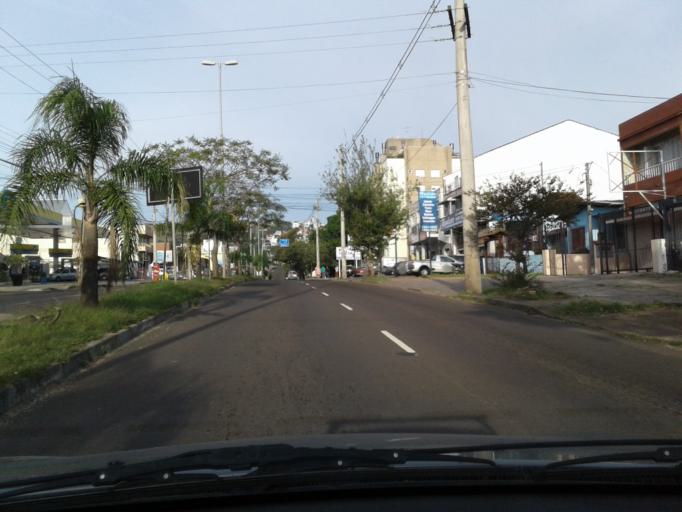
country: BR
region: Rio Grande do Sul
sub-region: Porto Alegre
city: Porto Alegre
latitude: -30.0927
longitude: -51.2336
